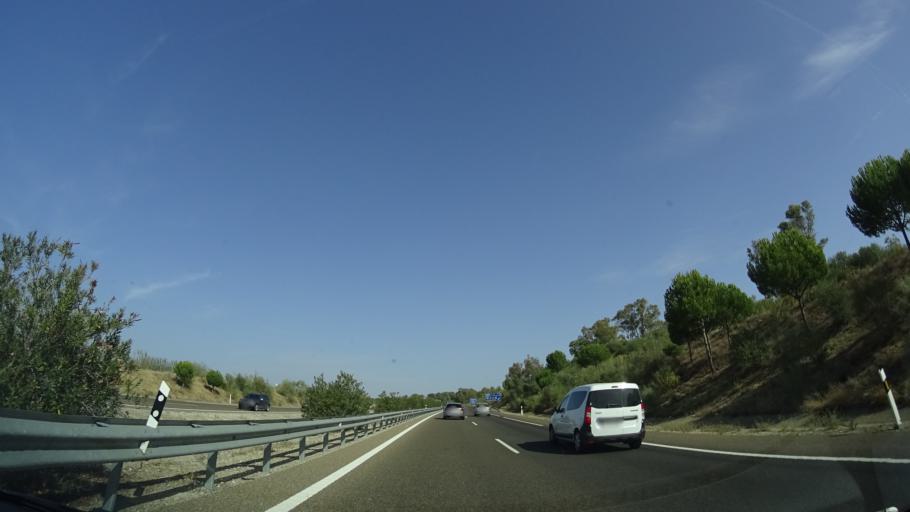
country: ES
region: Andalusia
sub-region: Provincia de Sevilla
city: Guillena
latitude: 37.5580
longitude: -6.1035
